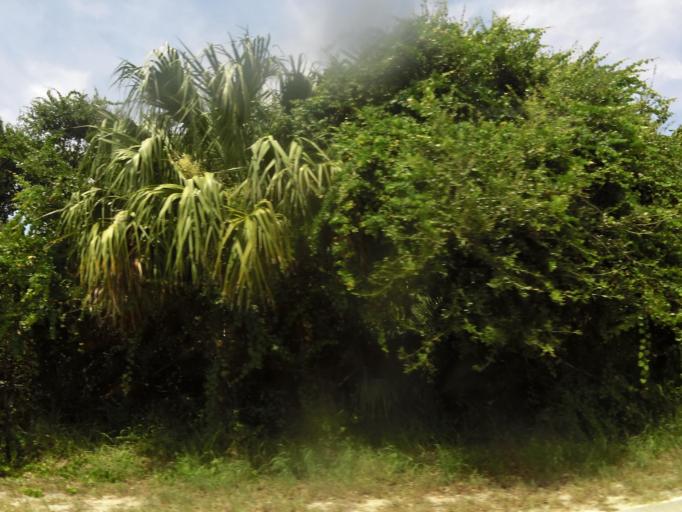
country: US
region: Florida
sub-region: Volusia County
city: Ponce Inlet
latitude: 29.0841
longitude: -80.9279
